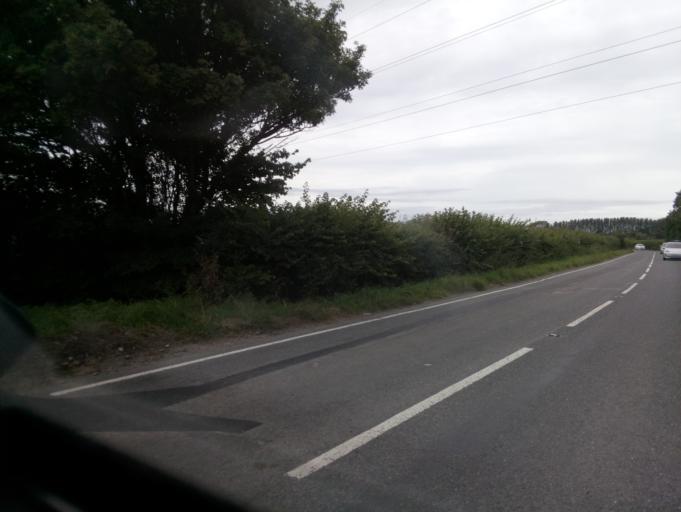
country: GB
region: England
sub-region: North Somerset
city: Churchill
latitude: 51.3557
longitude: -2.7884
